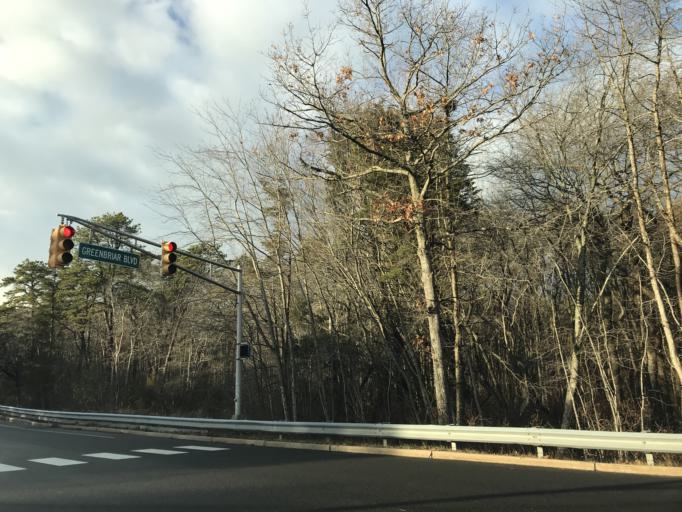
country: US
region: New Jersey
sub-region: Ocean County
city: Waretown
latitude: 39.7928
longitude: -74.2202
